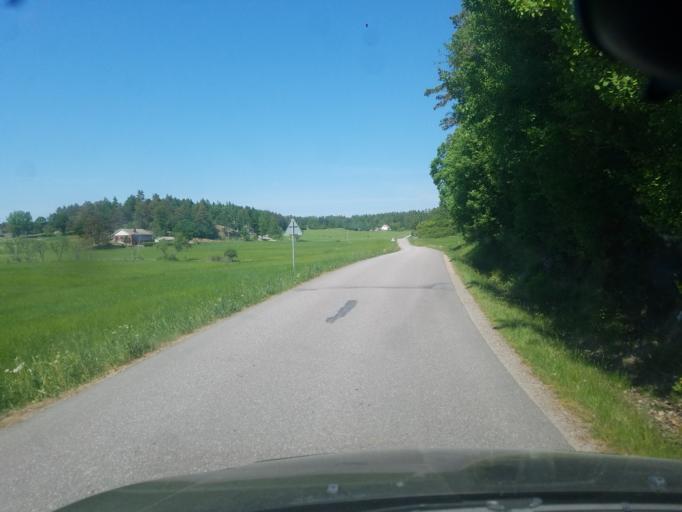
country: SE
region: Vaestra Goetaland
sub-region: Orust
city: Henan
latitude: 58.2775
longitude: 11.5765
